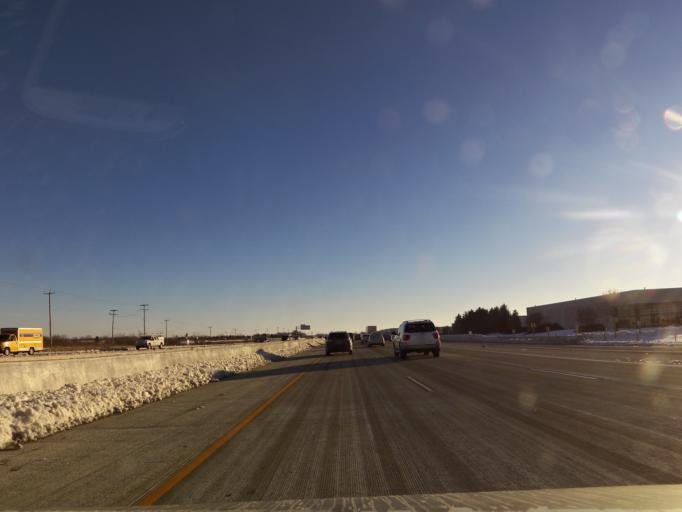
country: US
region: Wisconsin
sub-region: Racine County
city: Franksville
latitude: 42.7223
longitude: -87.9541
